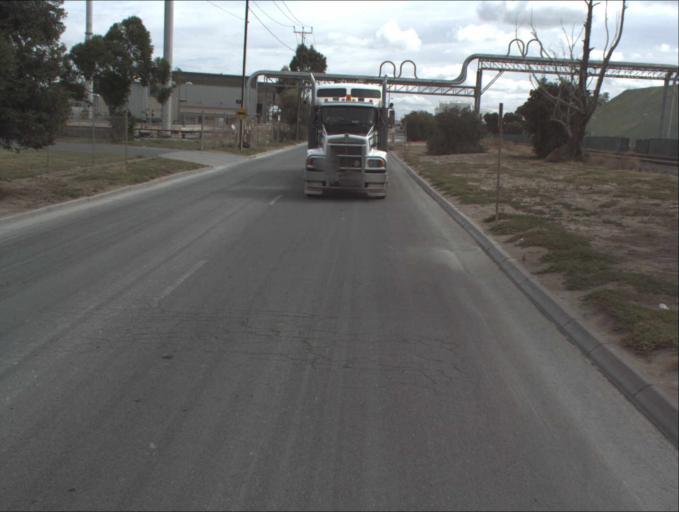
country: AU
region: South Australia
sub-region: Port Adelaide Enfield
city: Birkenhead
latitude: -34.8300
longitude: 138.5041
